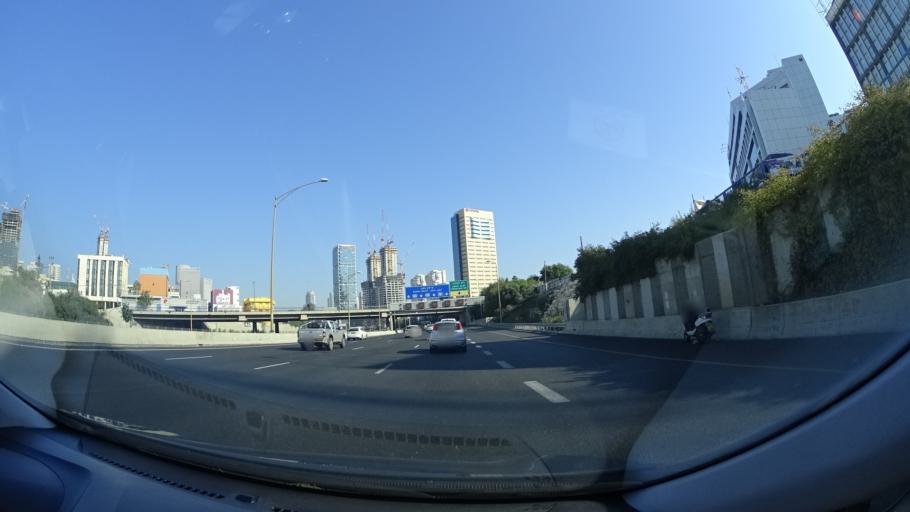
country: IL
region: Tel Aviv
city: Tel Aviv
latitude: 32.0635
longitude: 34.7890
